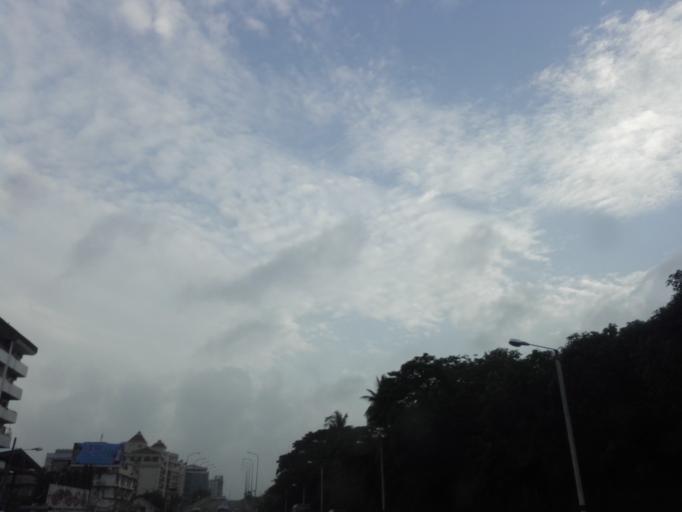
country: MM
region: Yangon
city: Yangon
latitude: 16.8226
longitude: 96.1318
